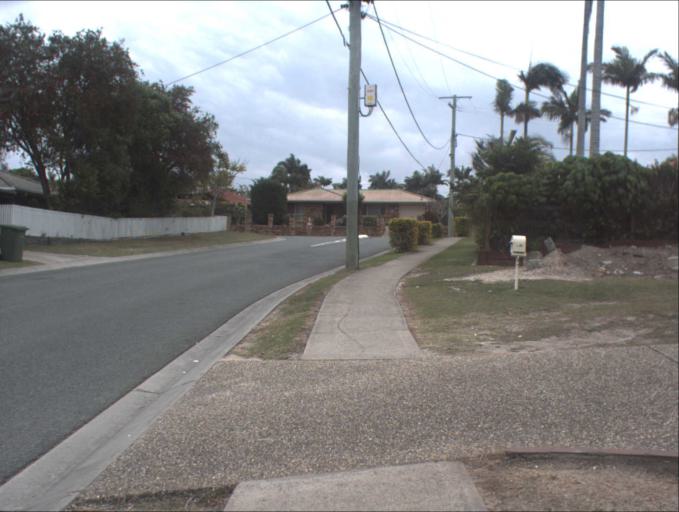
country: AU
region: Queensland
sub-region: Logan
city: Park Ridge South
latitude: -27.6797
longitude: 153.0502
